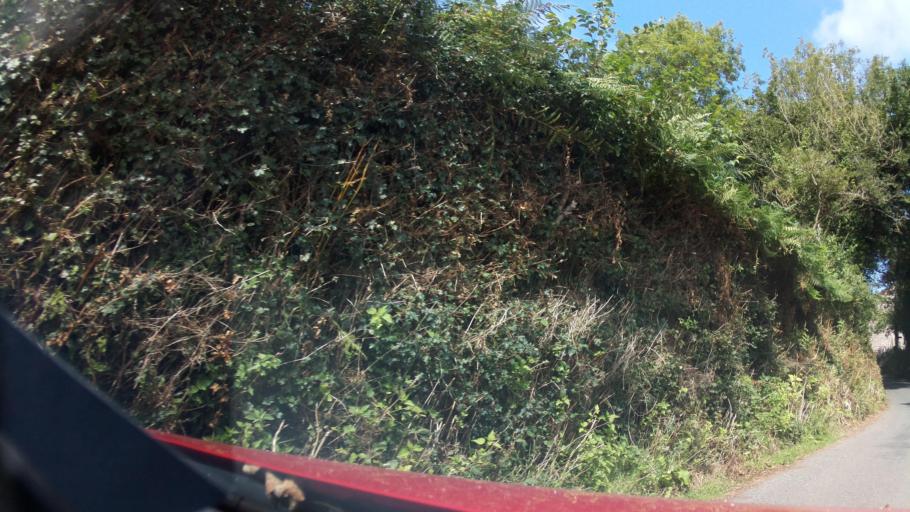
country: GB
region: England
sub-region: Devon
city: Marldon
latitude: 50.4072
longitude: -3.6101
